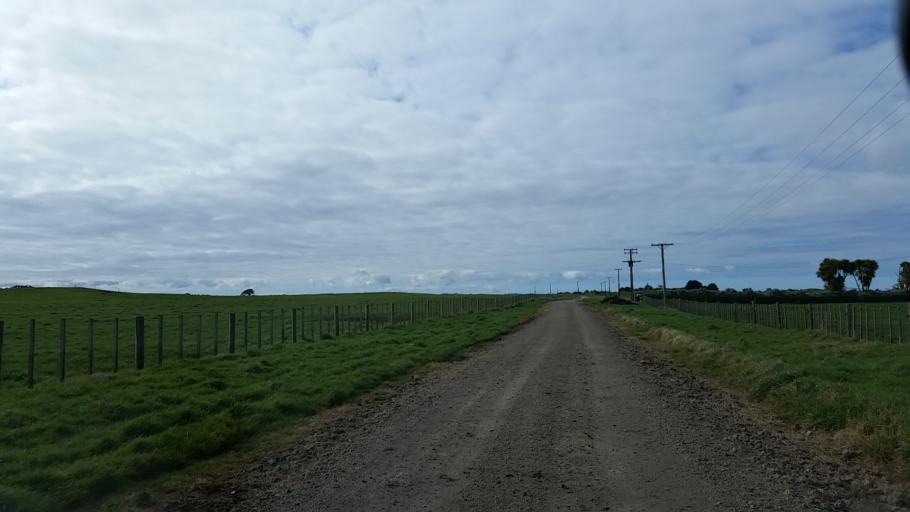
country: NZ
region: Taranaki
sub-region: South Taranaki District
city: Patea
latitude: -39.8071
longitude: 174.6493
